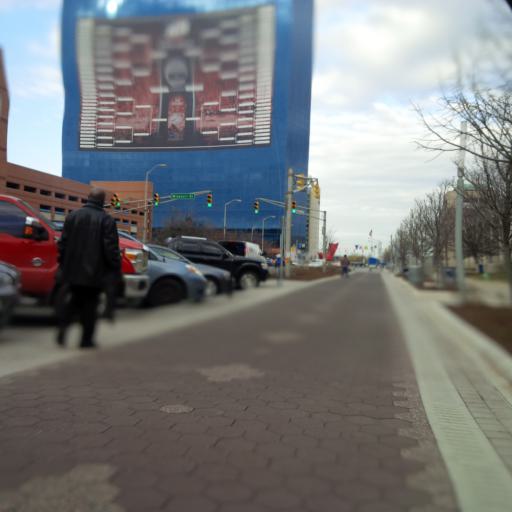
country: US
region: Indiana
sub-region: Marion County
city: Indianapolis
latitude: 39.7673
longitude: -86.1650
